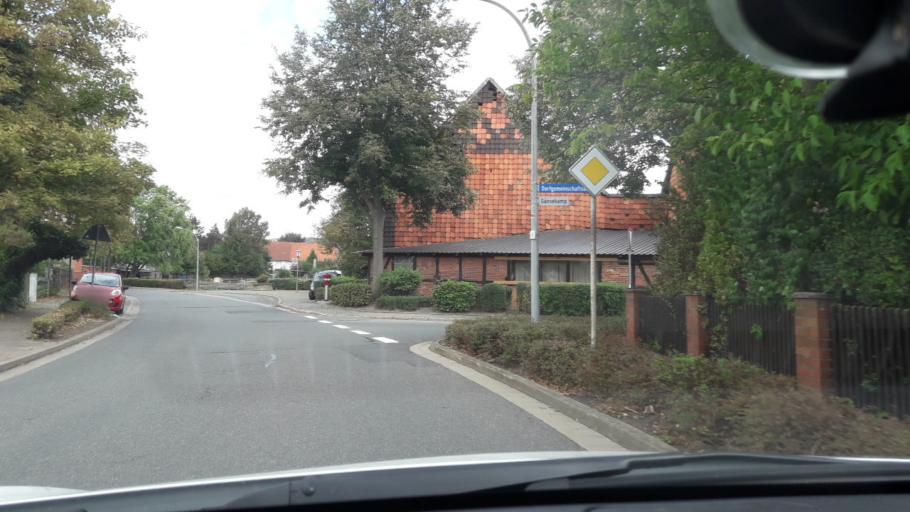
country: DE
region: Lower Saxony
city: Liebenburg
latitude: 51.9958
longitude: 10.4015
